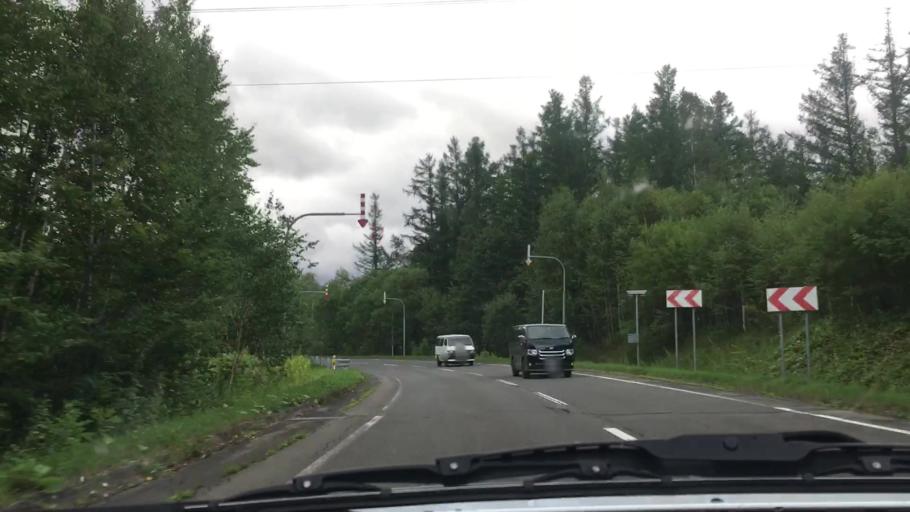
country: JP
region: Hokkaido
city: Shimo-furano
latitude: 43.0549
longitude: 142.6686
